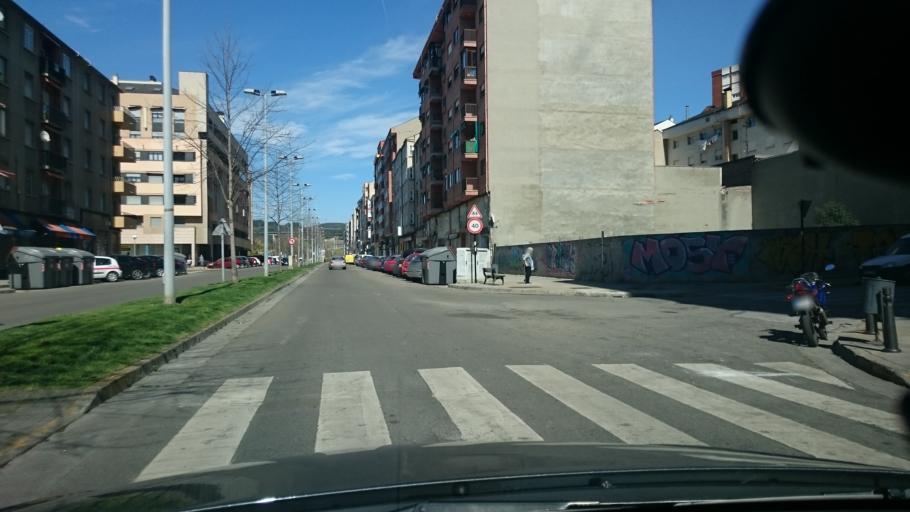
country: ES
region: Castille and Leon
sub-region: Provincia de Leon
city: Ponferrada
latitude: 42.5483
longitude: -6.5903
